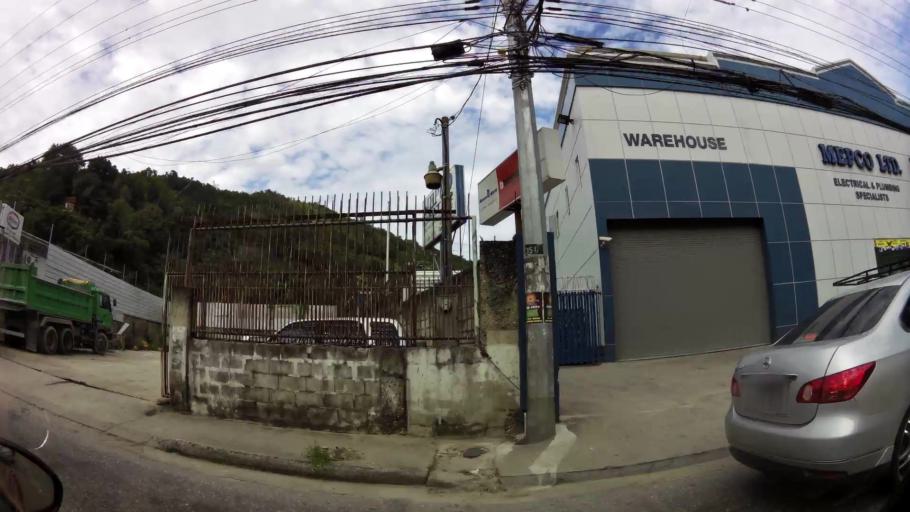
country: TT
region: Diego Martin
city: Petit Valley
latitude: 10.7063
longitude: -61.5117
